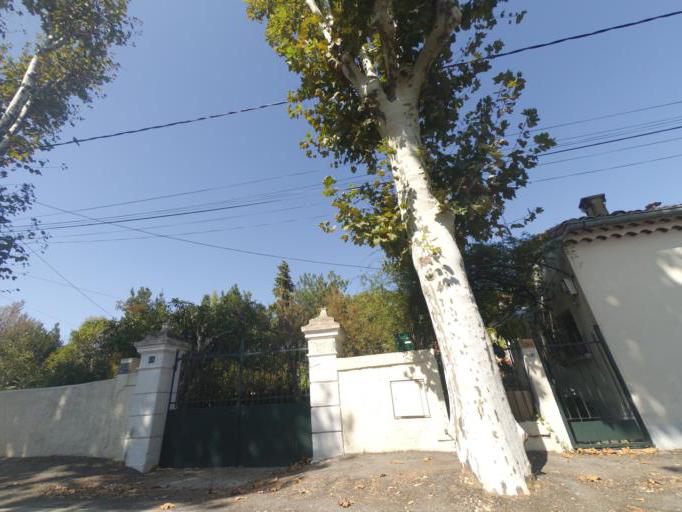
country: FR
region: Languedoc-Roussillon
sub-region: Departement du Gard
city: Calvisson
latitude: 43.7887
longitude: 4.1986
